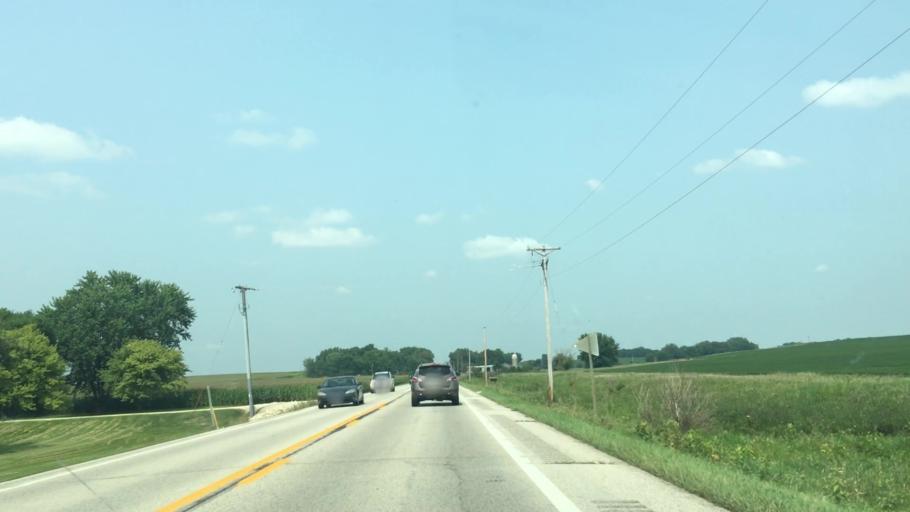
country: US
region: Iowa
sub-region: Buchanan County
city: Independence
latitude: 42.5232
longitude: -91.8898
